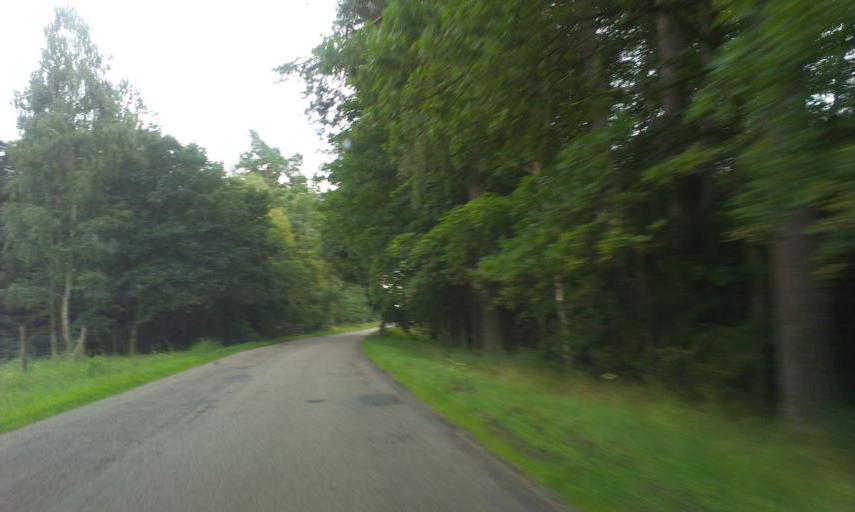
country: PL
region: West Pomeranian Voivodeship
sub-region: Powiat bialogardzki
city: Tychowo
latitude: 53.9609
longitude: 16.2224
